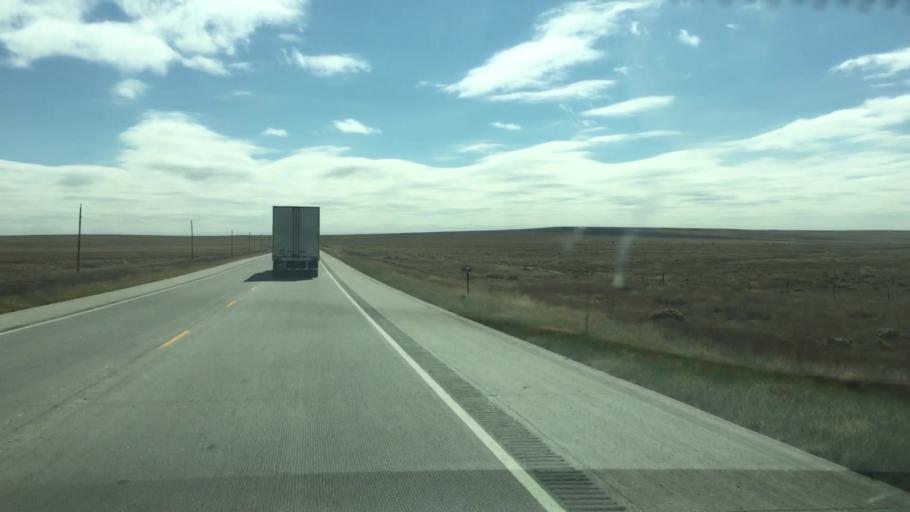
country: US
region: Colorado
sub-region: Lincoln County
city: Hugo
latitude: 39.0337
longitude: -103.3281
